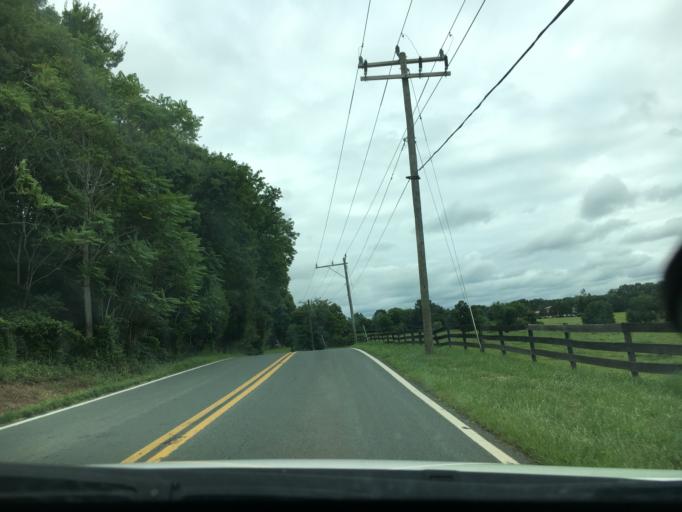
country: US
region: Virginia
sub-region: City of Charlottesville
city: Charlottesville
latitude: 37.9935
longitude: -78.4478
